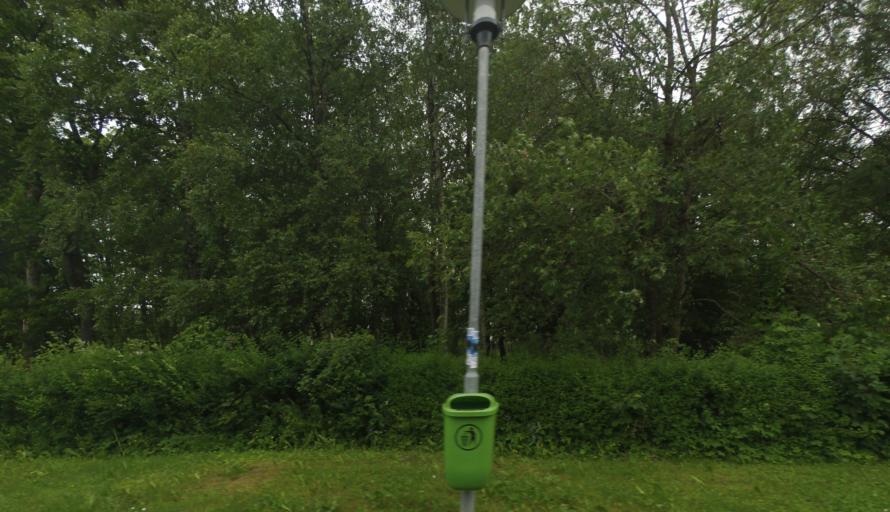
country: DE
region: Bavaria
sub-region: Upper Franconia
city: Weissenstadt
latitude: 50.0997
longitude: 11.8860
